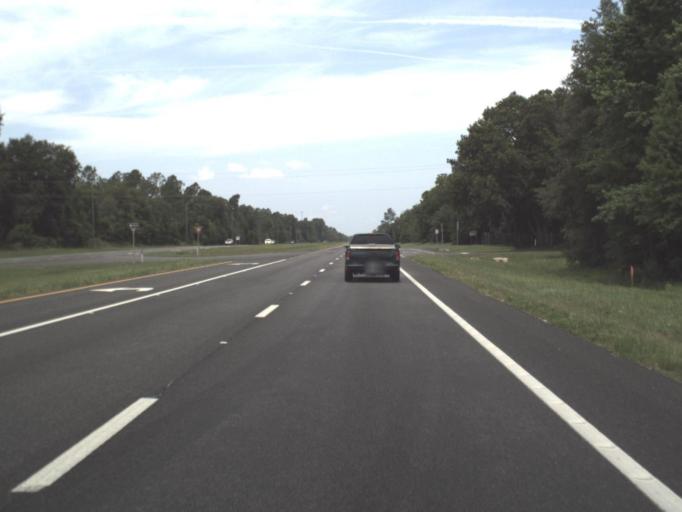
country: US
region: Florida
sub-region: Alachua County
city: Hawthorne
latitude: 29.6004
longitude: -82.1940
